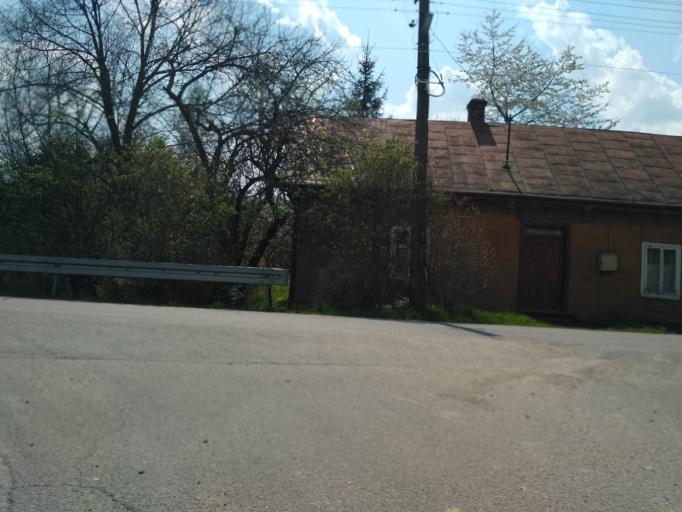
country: PL
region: Subcarpathian Voivodeship
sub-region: Powiat jasielski
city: Tarnowiec
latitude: 49.7353
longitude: 21.6048
